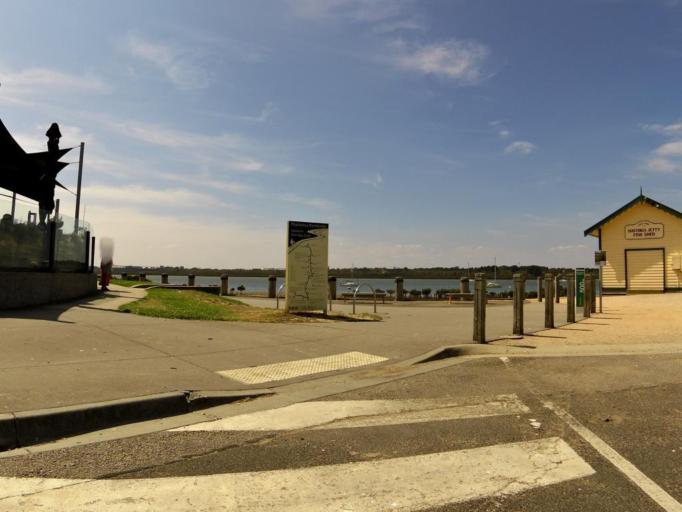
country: AU
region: Victoria
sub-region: Mornington Peninsula
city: Hastings
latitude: -38.3085
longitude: 145.1975
